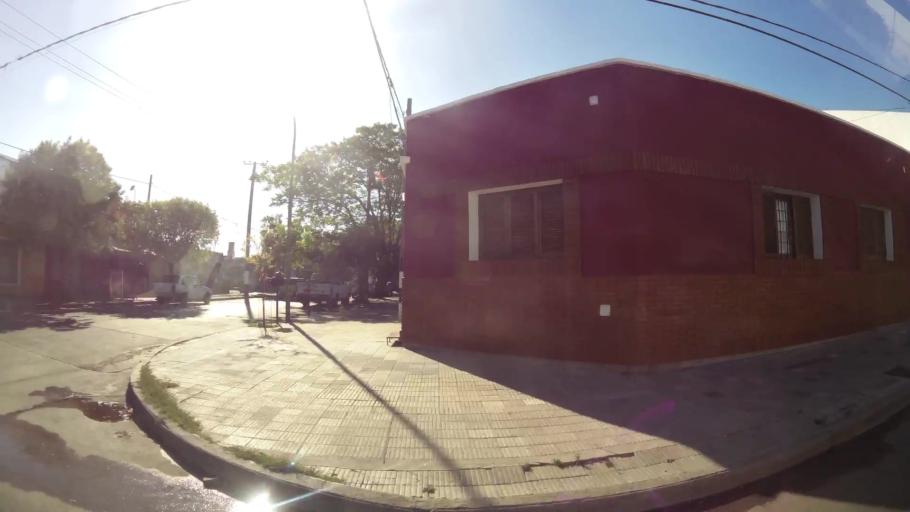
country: AR
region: Cordoba
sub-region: Departamento de Capital
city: Cordoba
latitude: -31.3895
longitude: -64.1670
